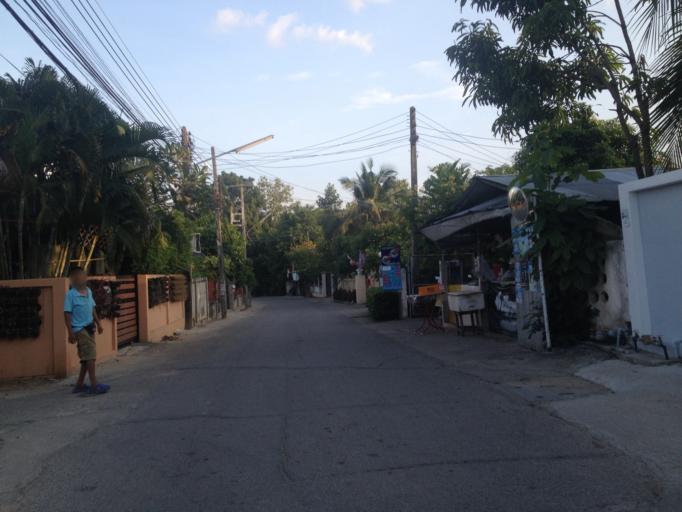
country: TH
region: Chiang Mai
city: Chiang Mai
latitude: 18.7639
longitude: 98.9419
